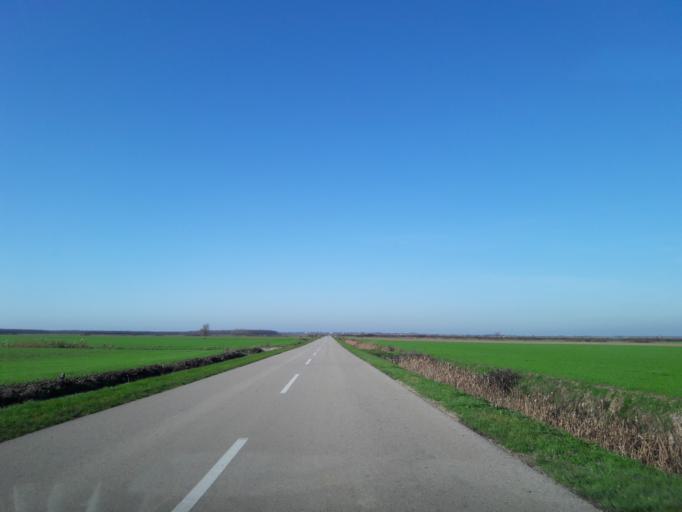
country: HR
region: Vukovarsko-Srijemska
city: Retkovci
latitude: 45.2444
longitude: 18.6397
